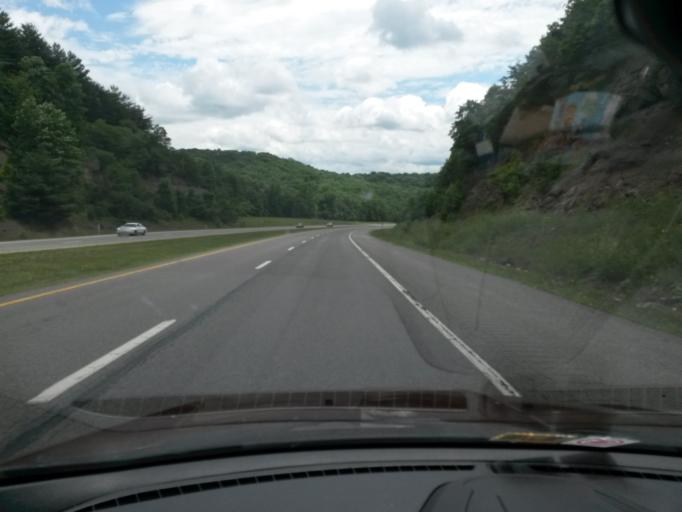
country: US
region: West Virginia
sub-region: Mercer County
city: Athens
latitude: 37.3535
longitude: -81.0180
